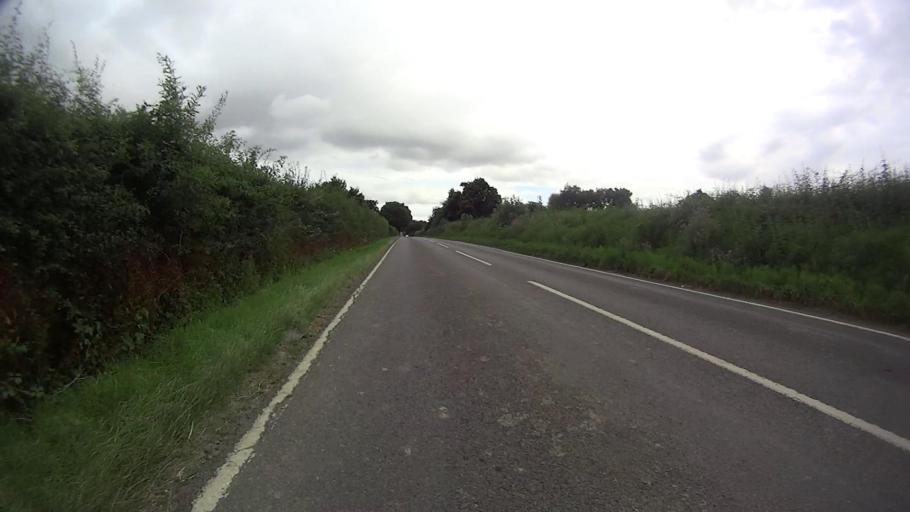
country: GB
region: England
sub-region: Surrey
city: Reigate
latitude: 51.1853
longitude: -0.2326
